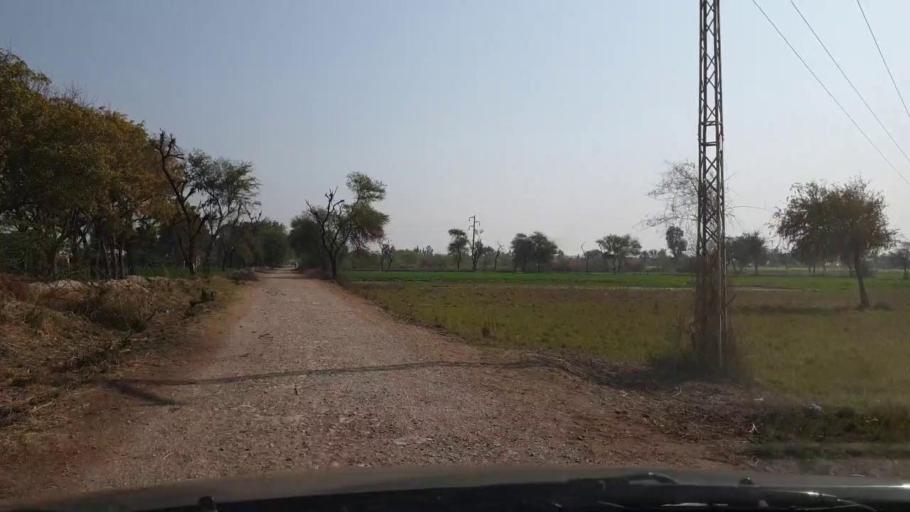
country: PK
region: Sindh
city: Jhol
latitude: 25.9345
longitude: 68.9938
